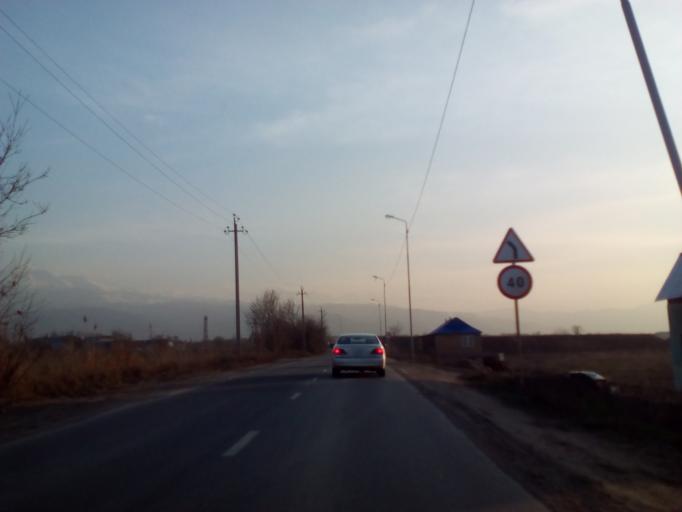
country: KZ
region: Almaty Oblysy
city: Burunday
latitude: 43.2356
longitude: 76.7417
